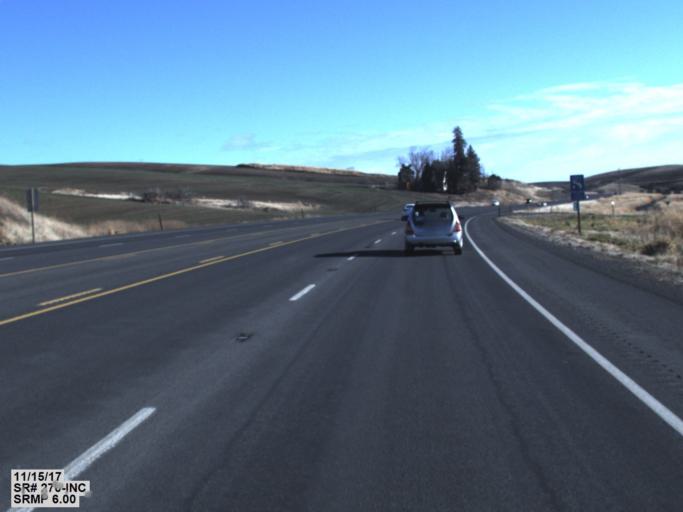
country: US
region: Washington
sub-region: Whitman County
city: Pullman
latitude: 46.7277
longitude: -117.1158
